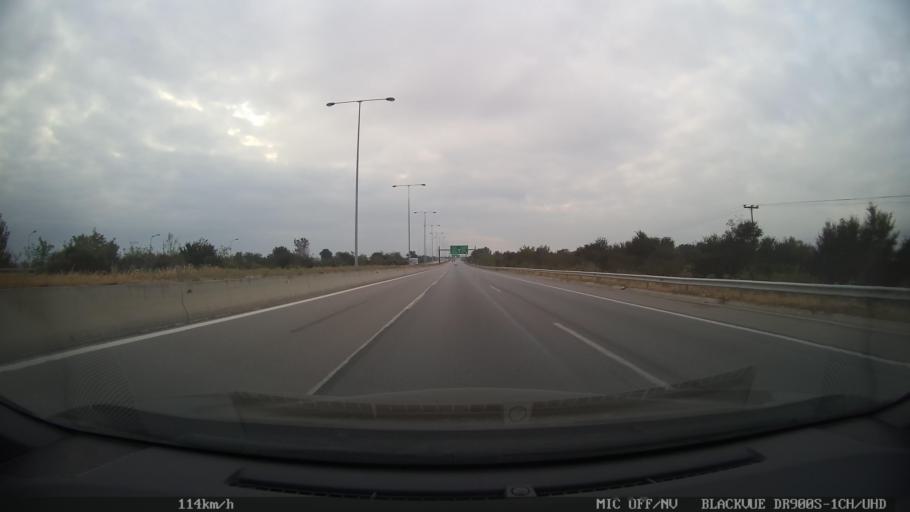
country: GR
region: Central Macedonia
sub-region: Nomos Thessalonikis
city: Nea Magnisia
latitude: 40.6643
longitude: 22.8369
